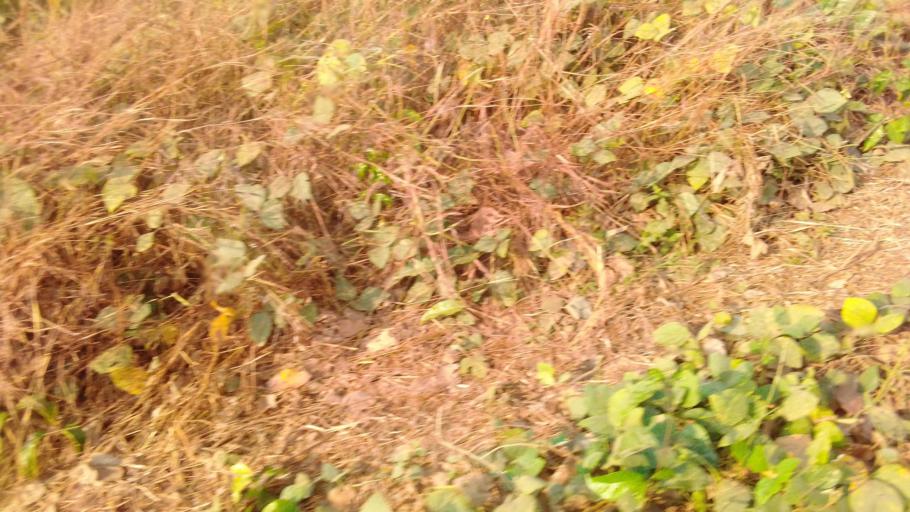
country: SL
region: Southern Province
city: Sumbuya
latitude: 7.6027
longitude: -12.1623
